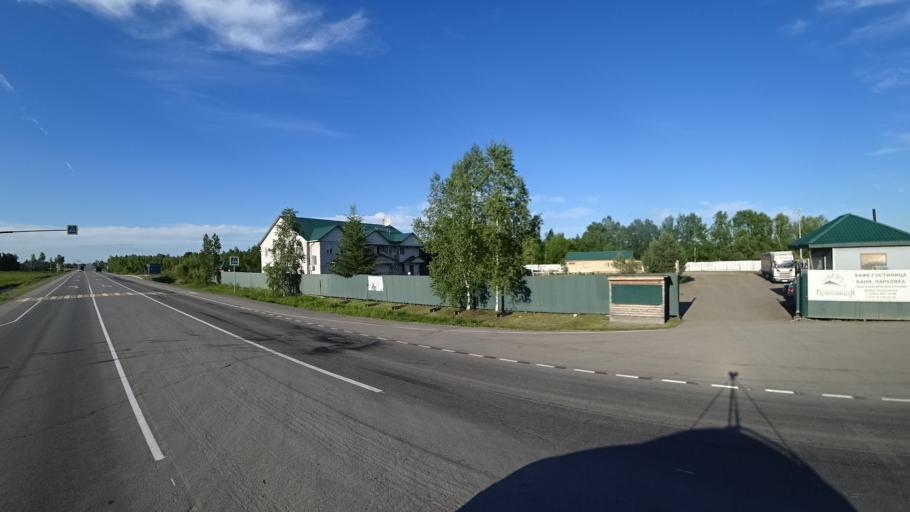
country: RU
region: Khabarovsk Krai
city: Khor
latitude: 47.8419
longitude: 134.9565
